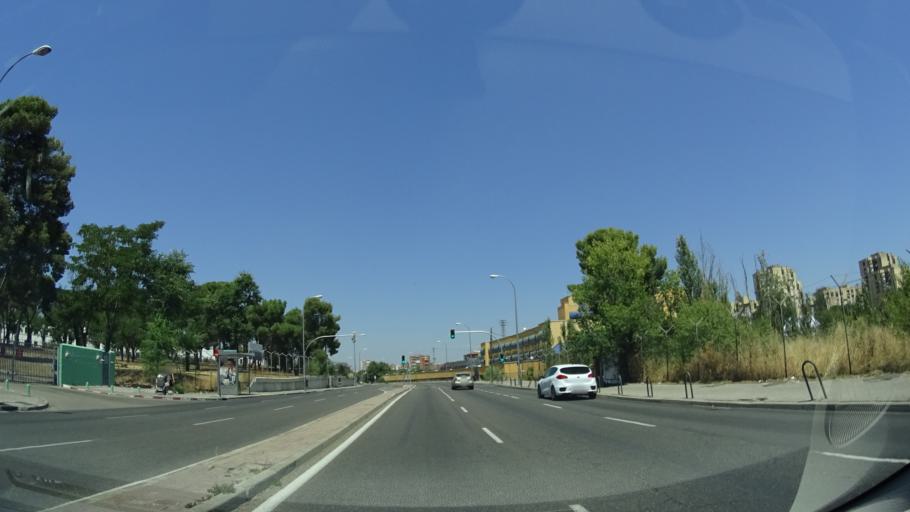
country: ES
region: Madrid
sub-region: Provincia de Madrid
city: Latina
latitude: 40.3816
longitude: -3.7575
